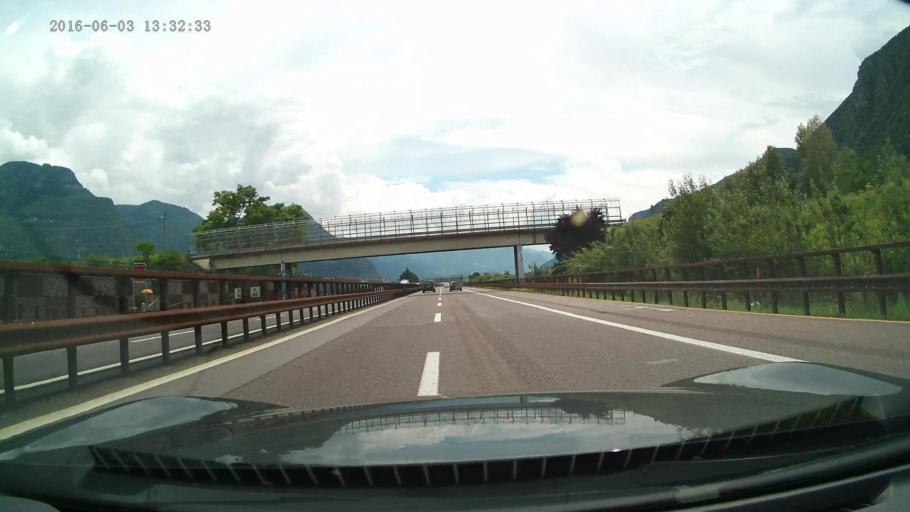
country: IT
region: Trentino-Alto Adige
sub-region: Bolzano
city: Laives
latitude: 46.4336
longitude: 11.3167
